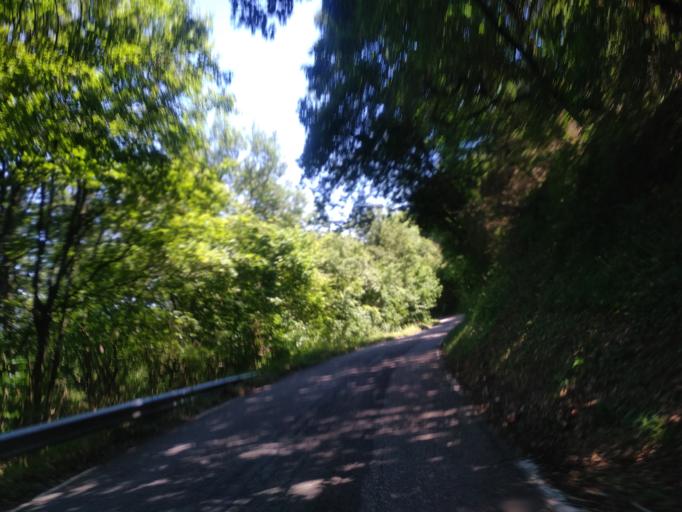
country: FR
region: Rhone-Alpes
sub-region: Departement du Rhone
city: Albigny-sur-Saone
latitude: 45.8525
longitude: 4.8205
